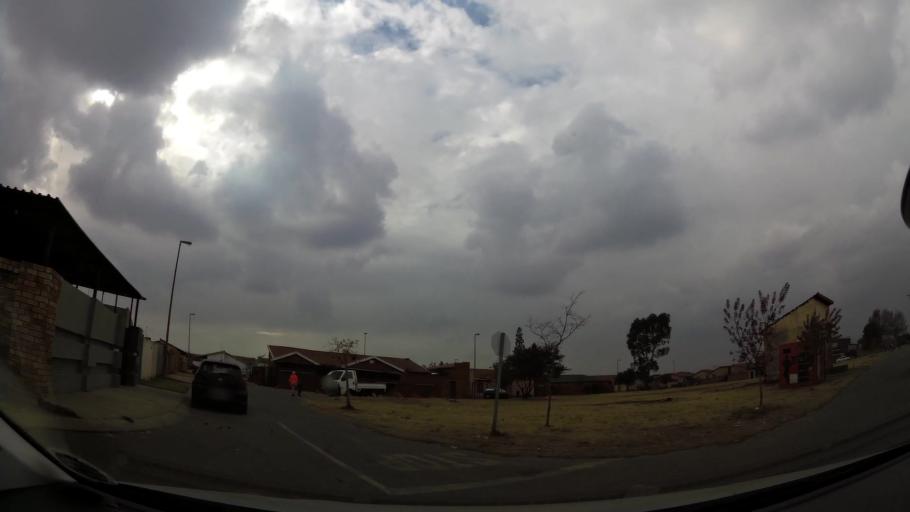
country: ZA
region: Gauteng
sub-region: City of Johannesburg Metropolitan Municipality
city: Soweto
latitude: -26.2592
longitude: 27.8570
